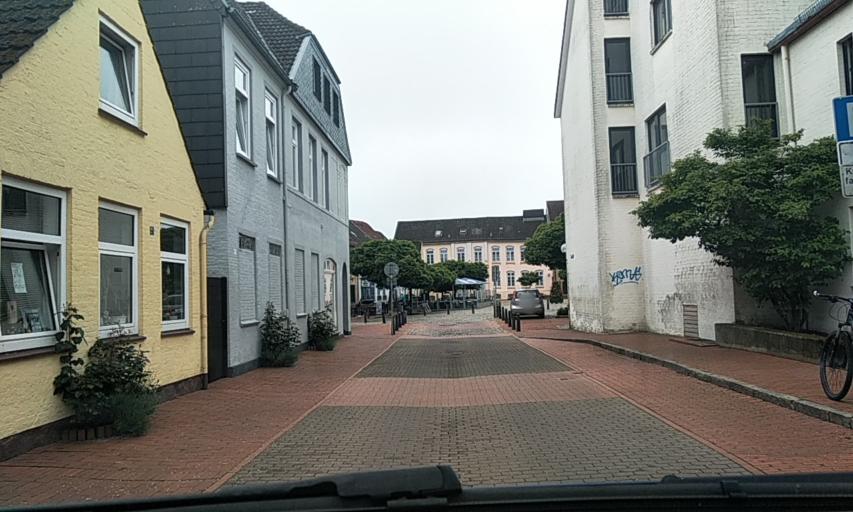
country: DE
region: Schleswig-Holstein
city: Schleswig
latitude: 54.5145
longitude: 9.5709
